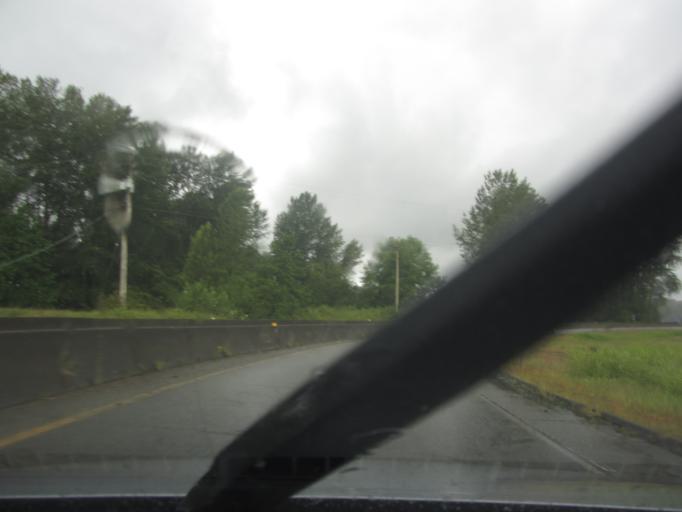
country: CA
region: British Columbia
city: Abbotsford
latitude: 49.1266
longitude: -122.3160
